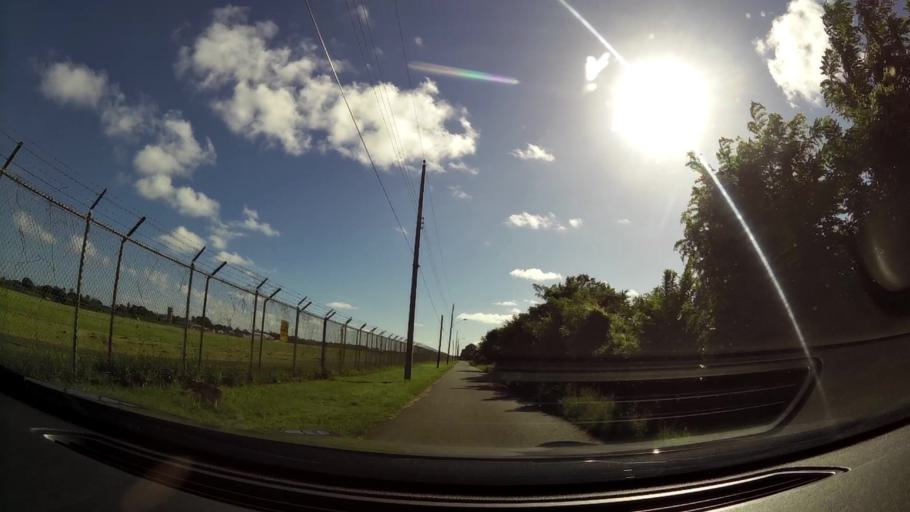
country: TT
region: Tobago
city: Scarborough
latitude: 11.1490
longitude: -60.8362
